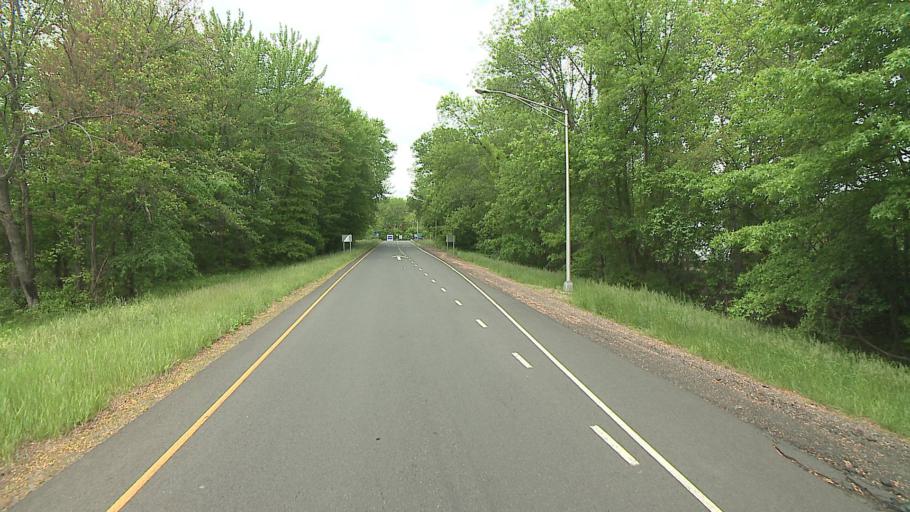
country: US
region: Connecticut
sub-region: Hartford County
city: Enfield
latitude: 41.9547
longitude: -72.5989
